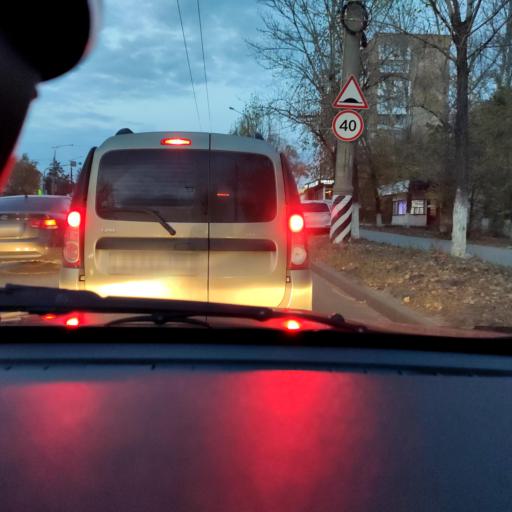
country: RU
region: Samara
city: Zhigulevsk
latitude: 53.4850
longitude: 49.4743
